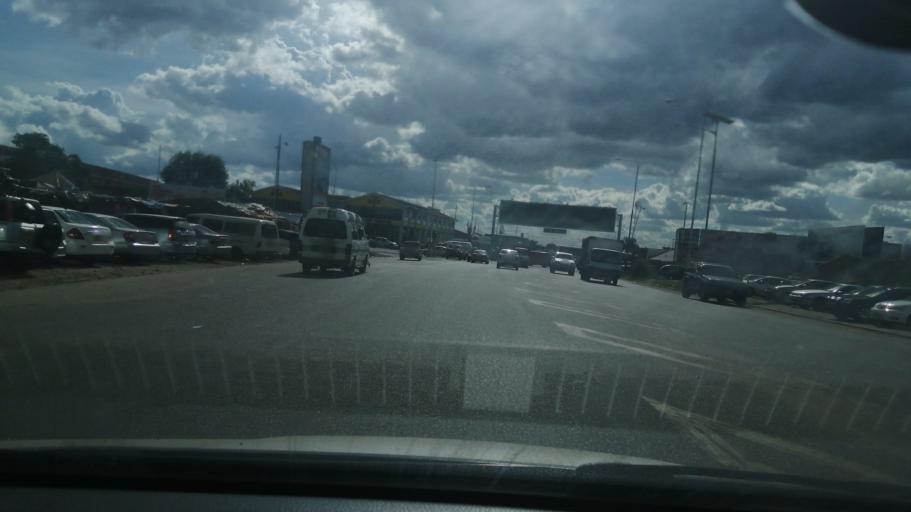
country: ZW
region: Harare
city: Harare
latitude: -17.8523
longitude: 31.0546
